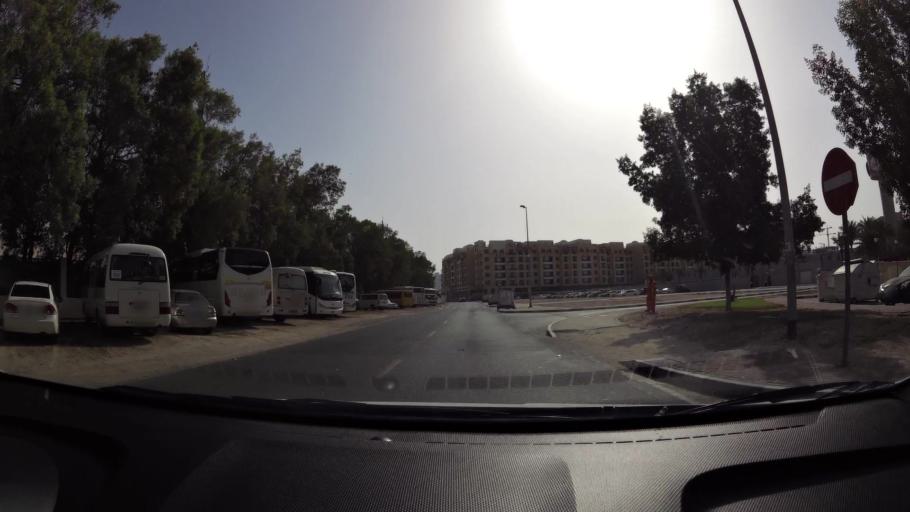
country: AE
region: Ash Shariqah
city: Sharjah
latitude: 25.2899
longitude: 55.3506
